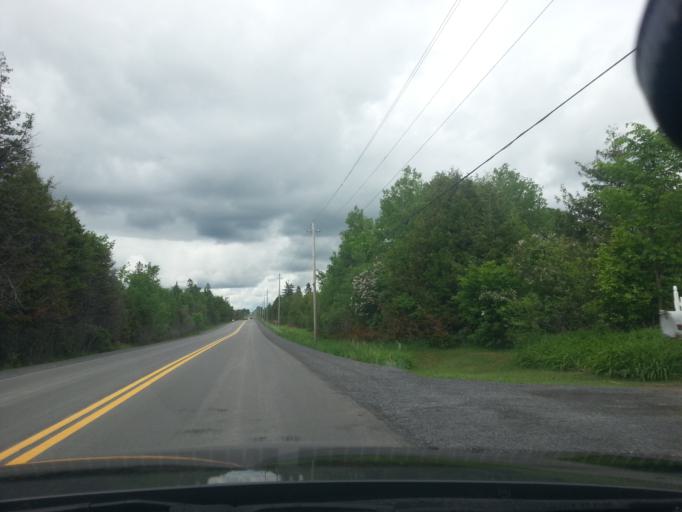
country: CA
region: Ontario
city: Carleton Place
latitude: 45.1817
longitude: -75.9926
